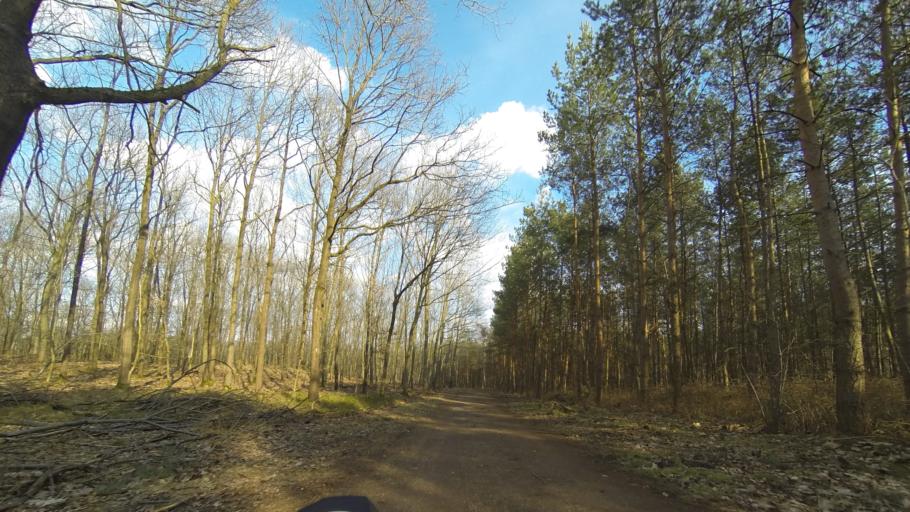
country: DE
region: Saxony
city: Moritzburg
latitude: 51.1484
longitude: 13.6391
